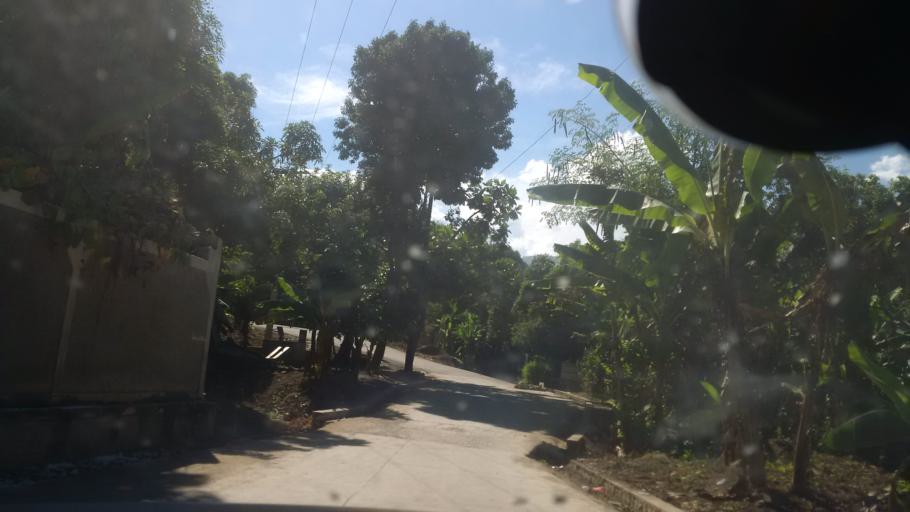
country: HT
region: Ouest
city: Grangwav
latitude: 18.4204
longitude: -72.7833
